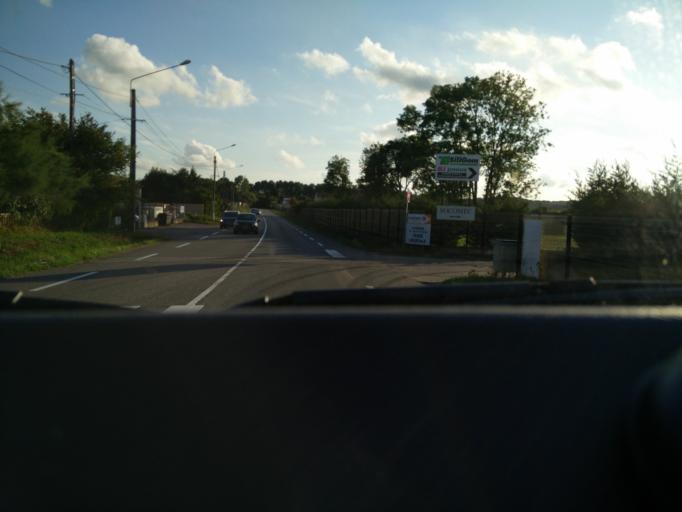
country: FR
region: Lorraine
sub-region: Departement de Meurthe-et-Moselle
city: Luneville
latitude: 48.5736
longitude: 6.4804
